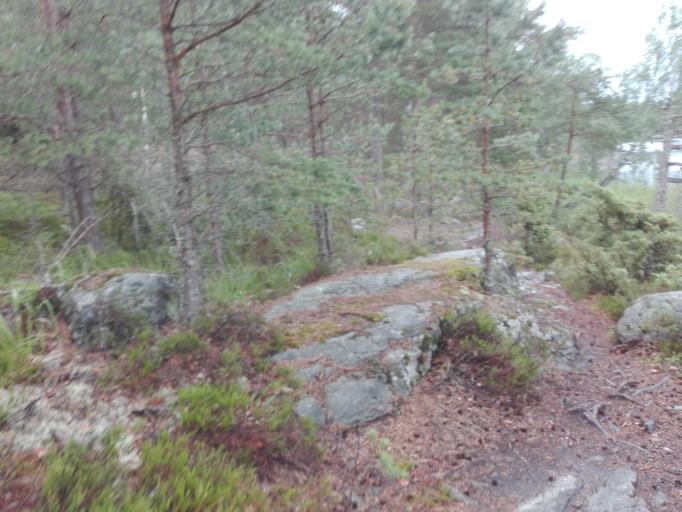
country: SE
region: Stockholm
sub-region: Nacka Kommun
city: Fisksatra
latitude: 59.2784
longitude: 18.2505
